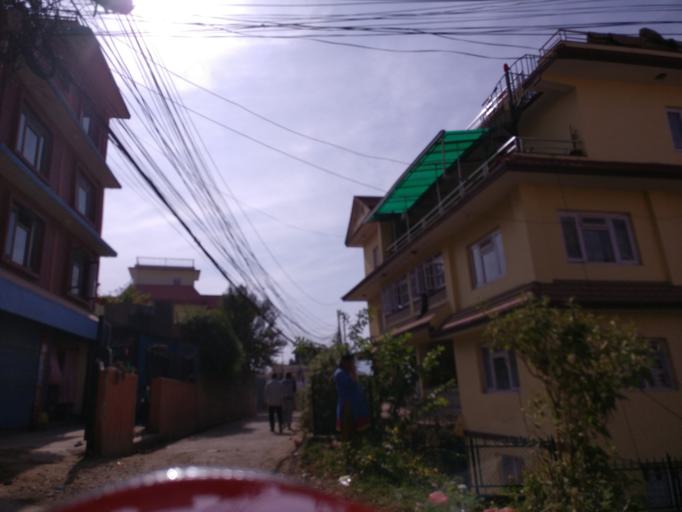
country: NP
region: Central Region
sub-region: Bagmati Zone
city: Patan
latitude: 27.6609
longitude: 85.3114
